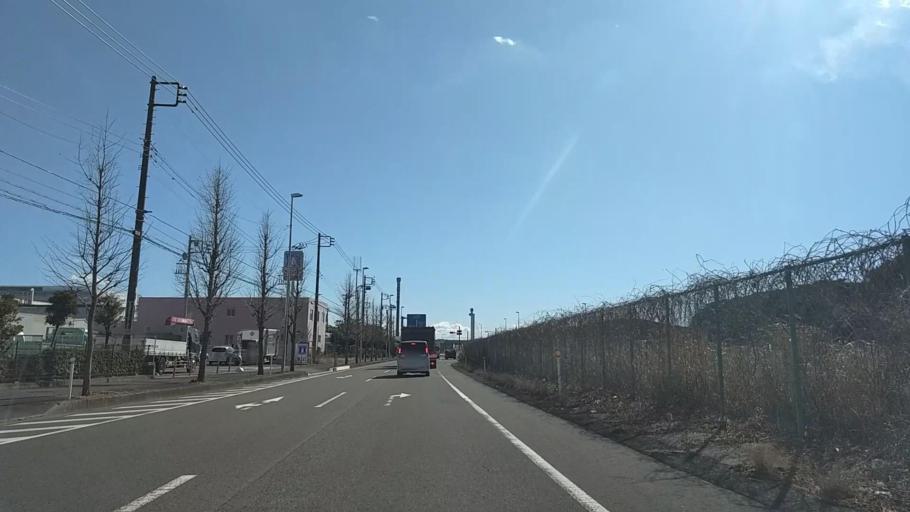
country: JP
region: Kanagawa
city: Yokosuka
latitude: 35.3476
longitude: 139.6445
